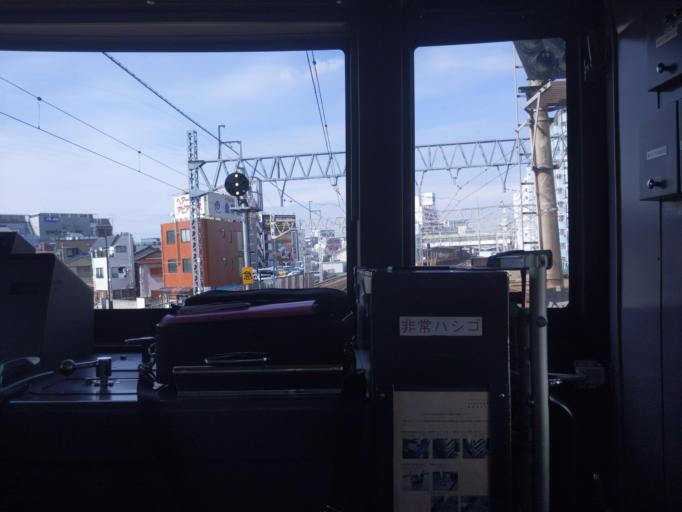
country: JP
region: Saitama
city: Soka
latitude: 35.7757
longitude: 139.7923
